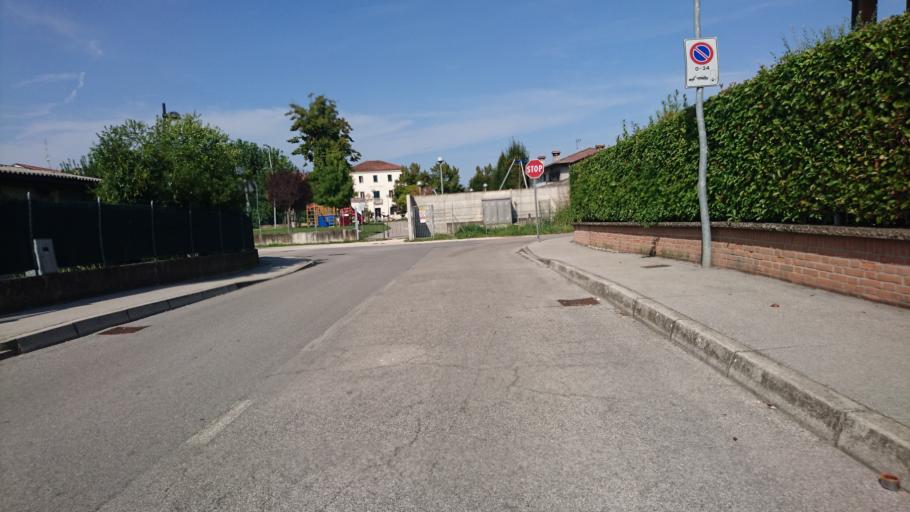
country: IT
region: Veneto
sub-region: Provincia di Padova
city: Veggiano
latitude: 45.4469
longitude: 11.7134
